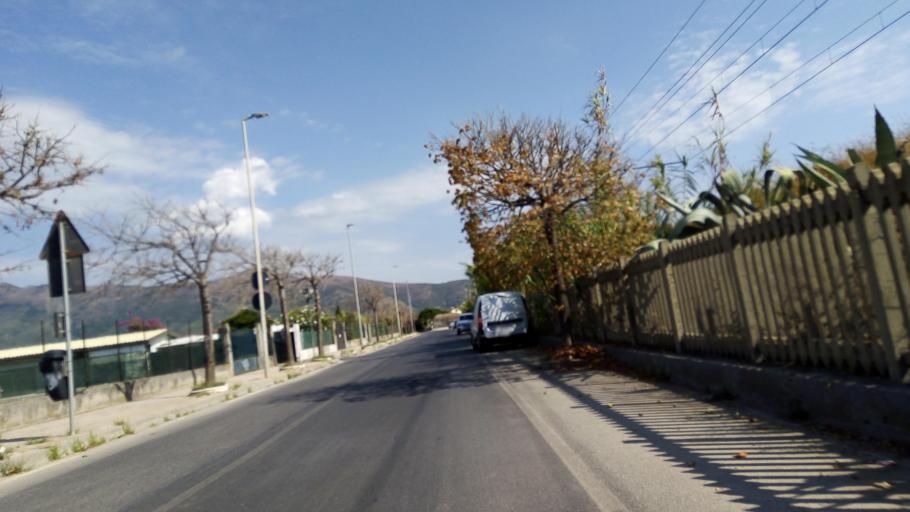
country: IT
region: Liguria
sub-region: Provincia di Savona
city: Albenga
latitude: 44.0687
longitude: 8.2252
